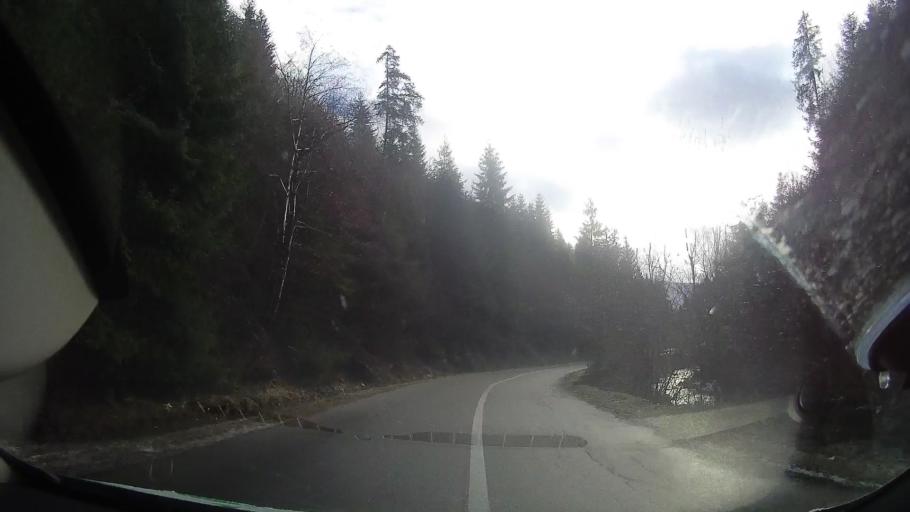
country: RO
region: Alba
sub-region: Comuna Albac
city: Albac
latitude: 46.4731
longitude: 22.9640
